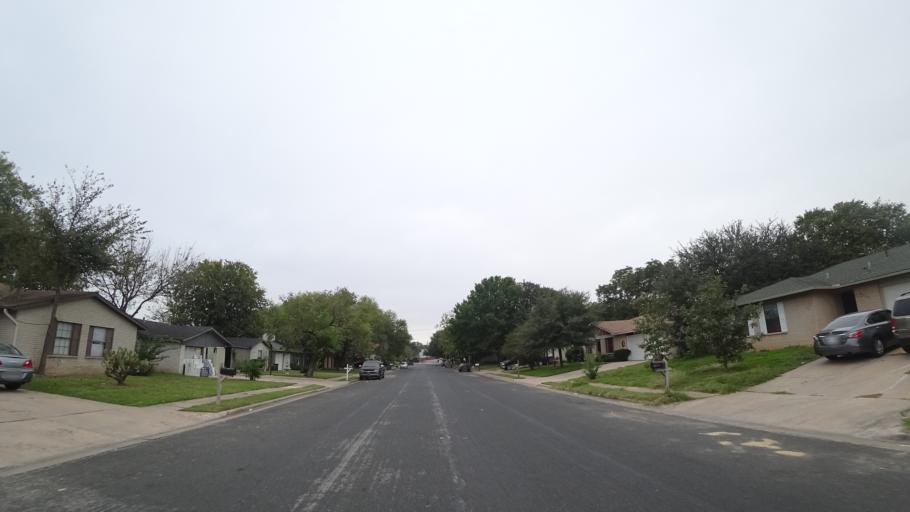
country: US
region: Texas
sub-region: Travis County
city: Onion Creek
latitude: 30.1950
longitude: -97.7794
